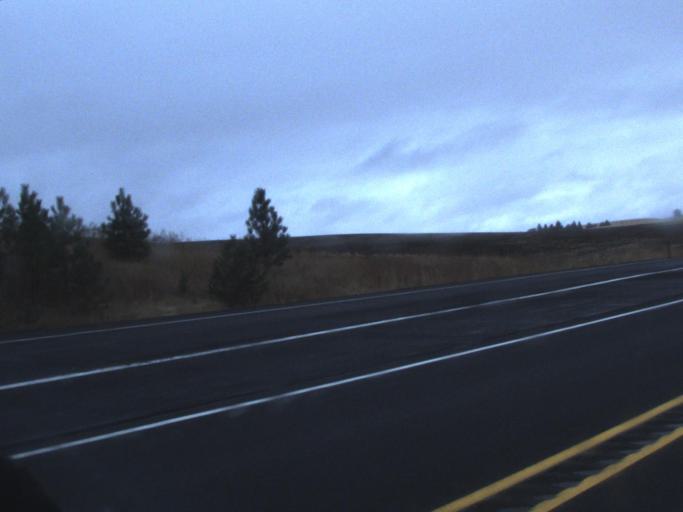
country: US
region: Washington
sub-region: Spokane County
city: Cheney
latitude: 47.3058
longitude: -117.3875
